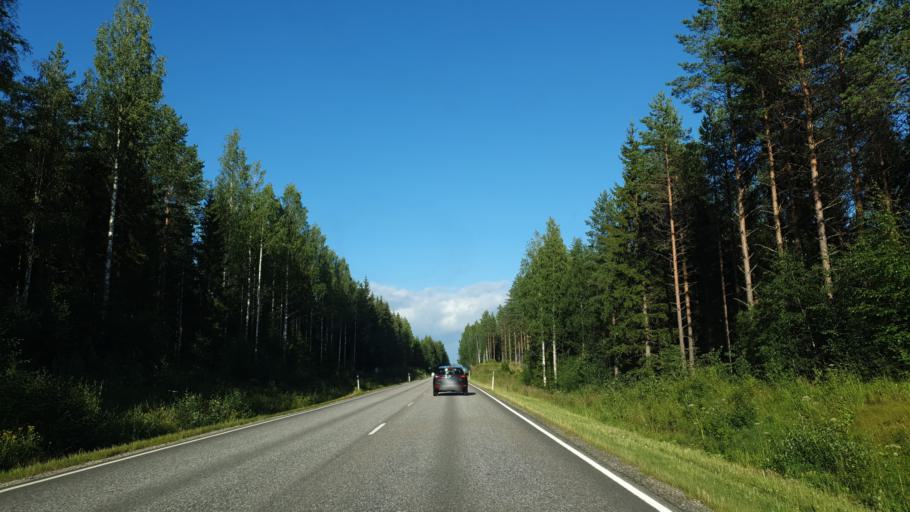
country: FI
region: North Karelia
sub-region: Joensuu
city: Outokumpu
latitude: 62.5203
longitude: 29.0260
